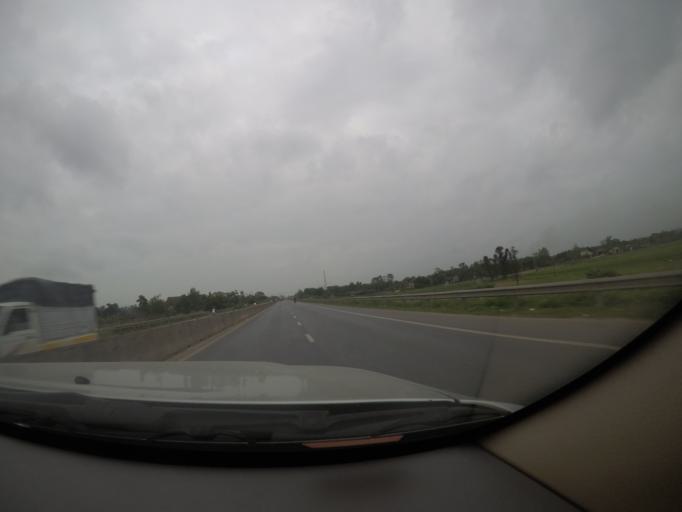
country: VN
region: Quang Tri
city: Hai Lang
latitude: 16.6944
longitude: 107.2361
